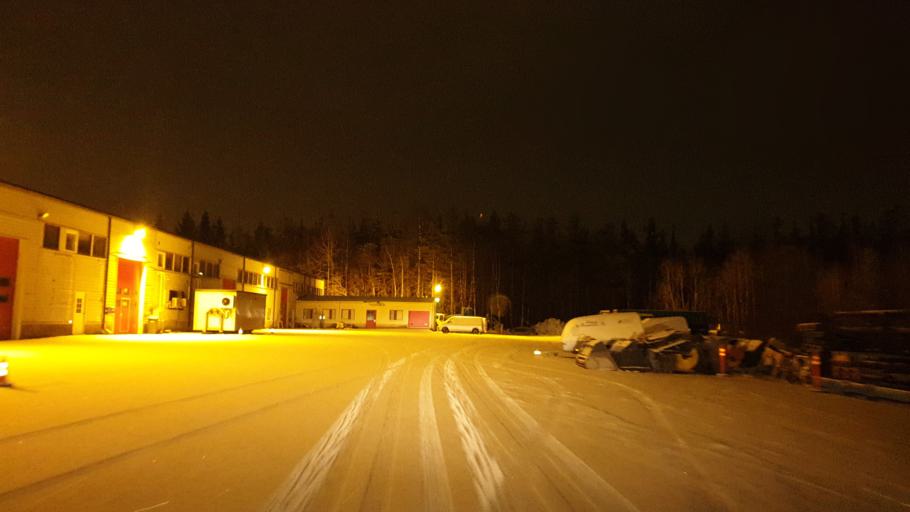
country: FI
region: Northern Ostrobothnia
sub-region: Oulu
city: Oulu
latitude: 64.9921
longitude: 25.4544
